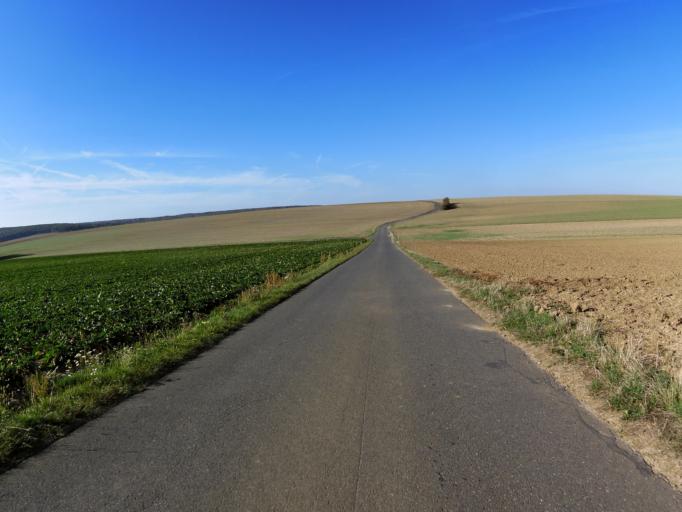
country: DE
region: Bavaria
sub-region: Regierungsbezirk Unterfranken
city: Reichenberg
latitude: 49.7185
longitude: 9.9344
